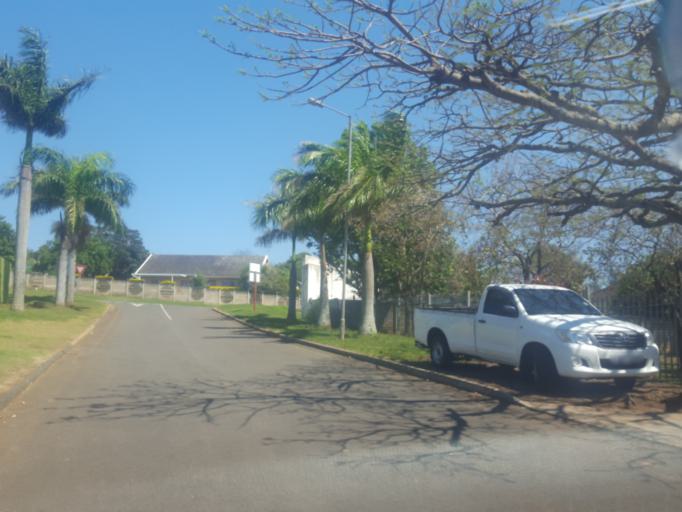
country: ZA
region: KwaZulu-Natal
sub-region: uThungulu District Municipality
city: Empangeni
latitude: -28.7600
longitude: 31.9056
